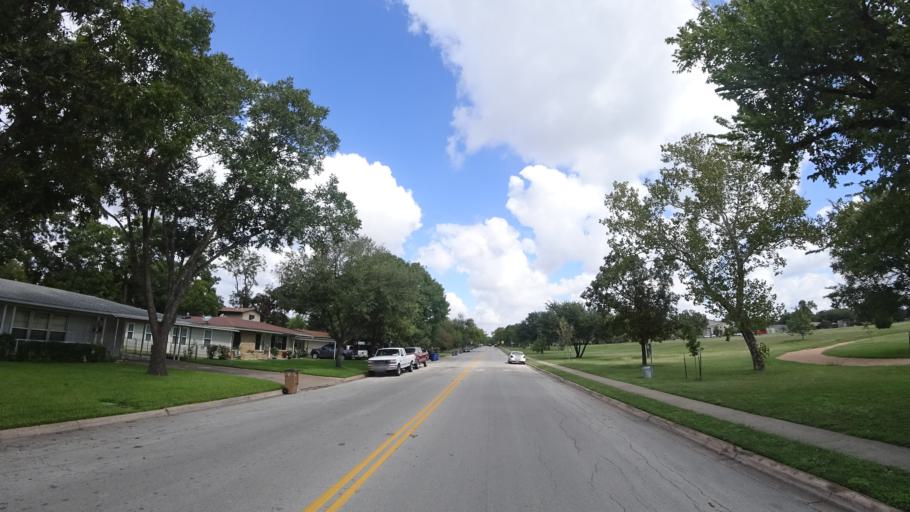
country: US
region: Texas
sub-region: Travis County
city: Austin
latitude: 30.3541
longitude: -97.7216
